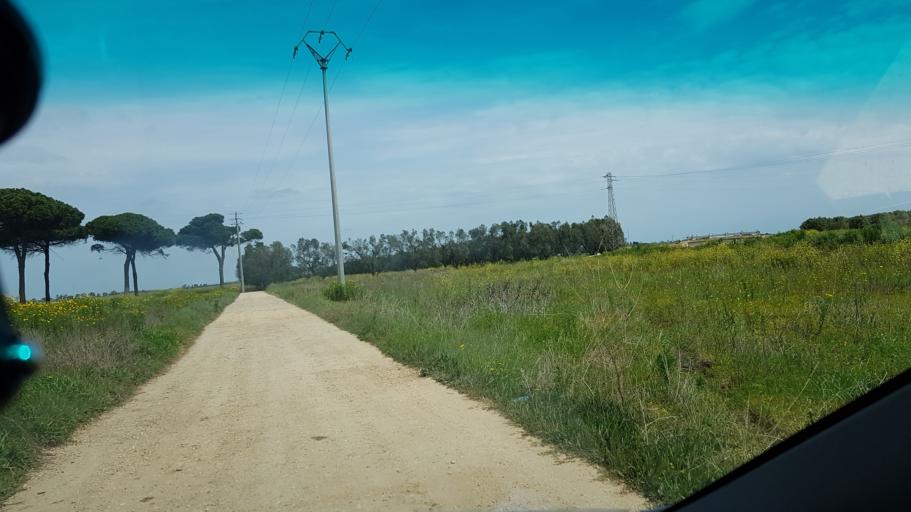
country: IT
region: Apulia
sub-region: Provincia di Brindisi
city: Mesagne
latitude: 40.6182
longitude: 17.8556
